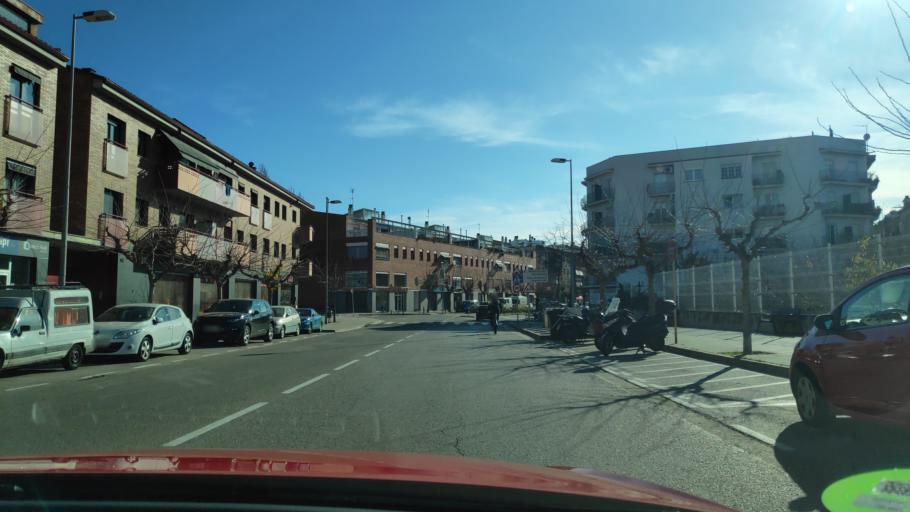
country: ES
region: Catalonia
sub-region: Provincia de Girona
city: Lloret de Mar
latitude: 41.7092
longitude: 2.8406
